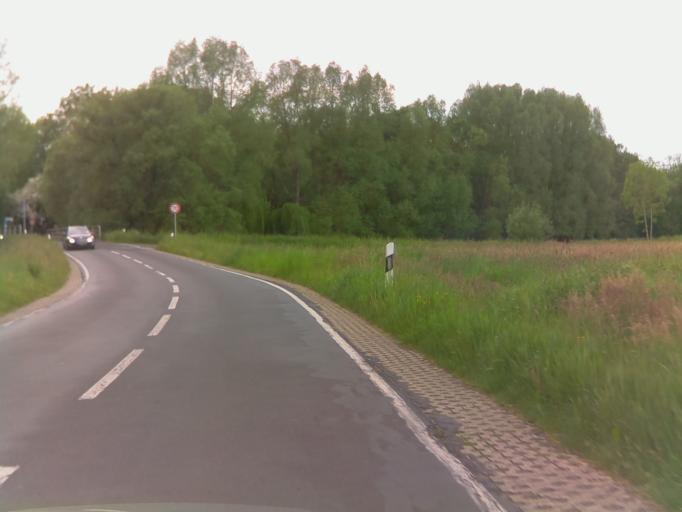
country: DE
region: Hesse
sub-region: Regierungsbezirk Kassel
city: Schrecksbach
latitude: 50.8834
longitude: 9.2593
